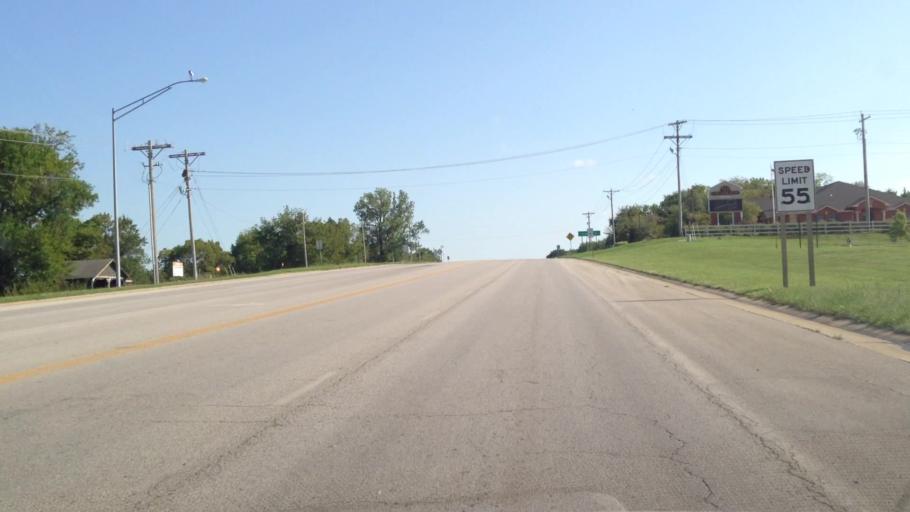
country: US
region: Kansas
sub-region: Bourbon County
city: Fort Scott
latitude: 37.8081
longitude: -94.7055
